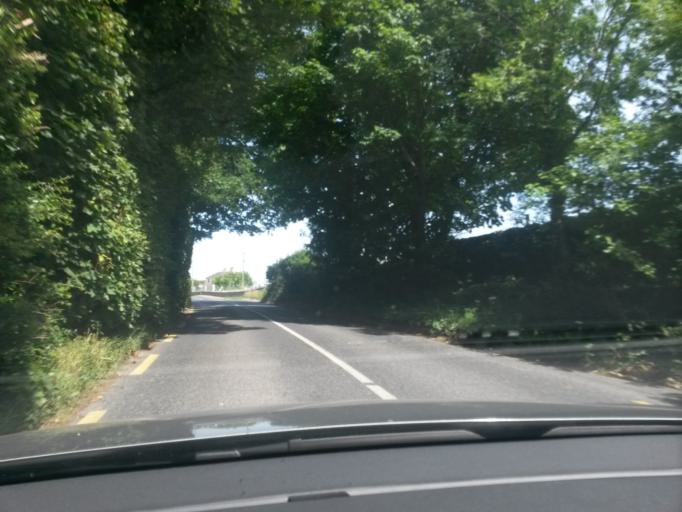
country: IE
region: Leinster
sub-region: Kildare
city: Eadestown
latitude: 53.2016
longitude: -6.5813
